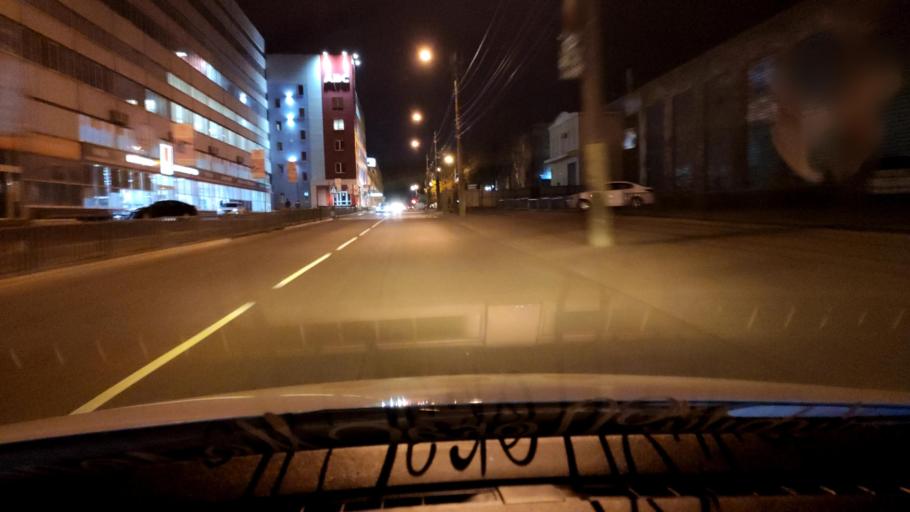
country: RU
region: Voronezj
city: Voronezh
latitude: 51.6814
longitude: 39.1712
